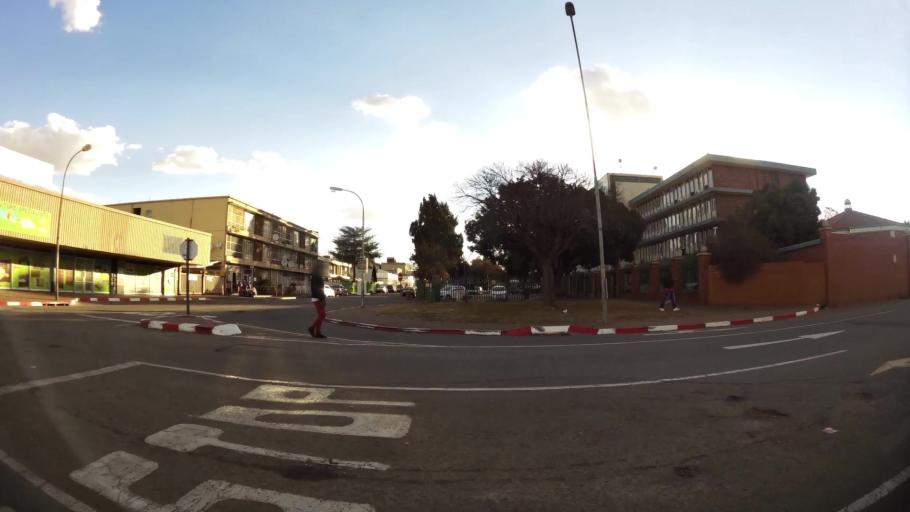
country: ZA
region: North-West
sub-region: Dr Kenneth Kaunda District Municipality
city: Potchefstroom
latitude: -26.7163
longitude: 27.0989
